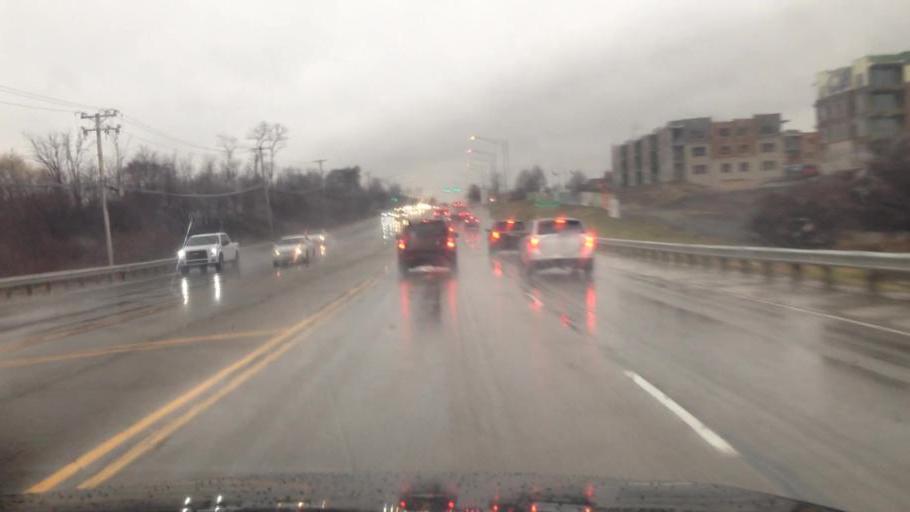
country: US
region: Illinois
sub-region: Kane County
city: Sleepy Hollow
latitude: 42.0975
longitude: -88.3352
